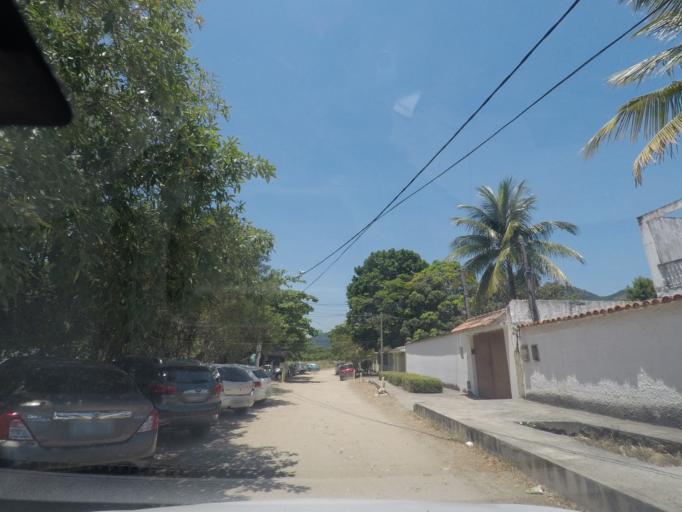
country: BR
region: Rio de Janeiro
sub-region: Niteroi
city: Niteroi
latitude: -22.9672
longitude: -43.0450
